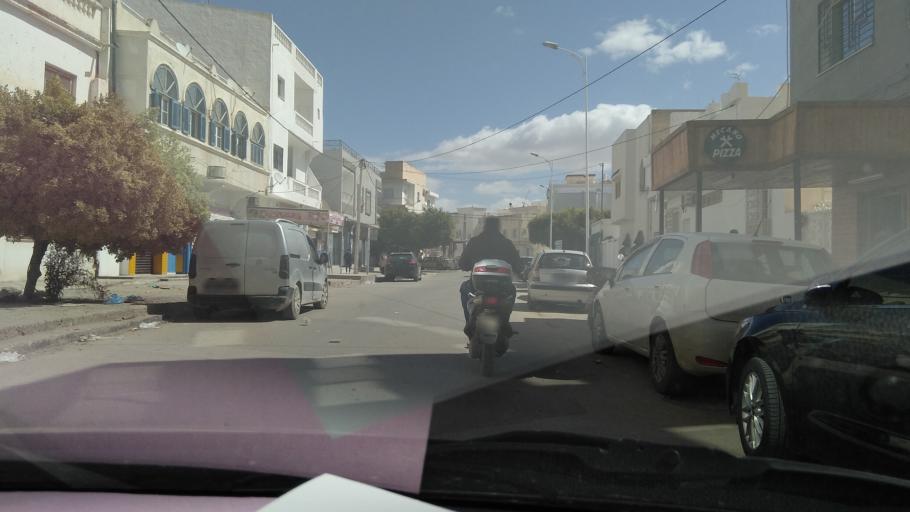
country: TN
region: Al Qayrawan
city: Kairouan
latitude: 35.6710
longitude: 10.1018
